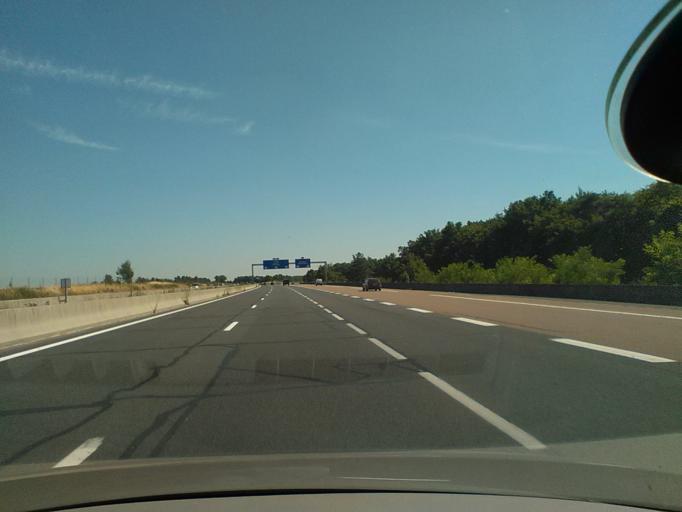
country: FR
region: Ile-de-France
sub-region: Departement de Seine-et-Marne
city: Souppes-sur-Loing
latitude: 48.2218
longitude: 2.7674
